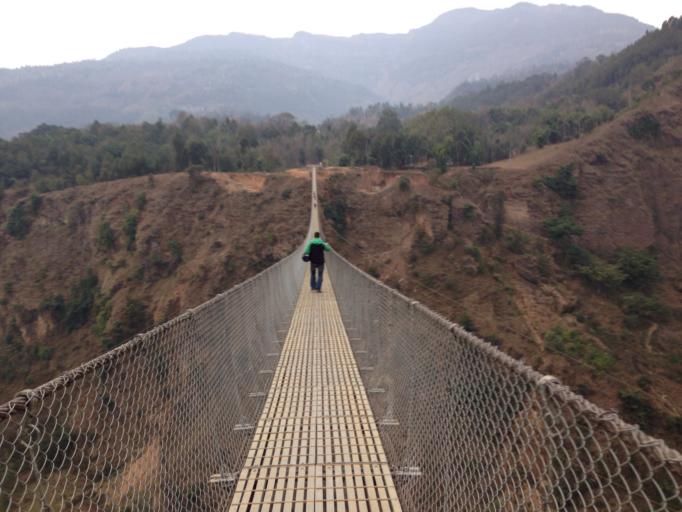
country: NP
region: Western Region
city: Baglung
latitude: 28.2047
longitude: 83.6712
